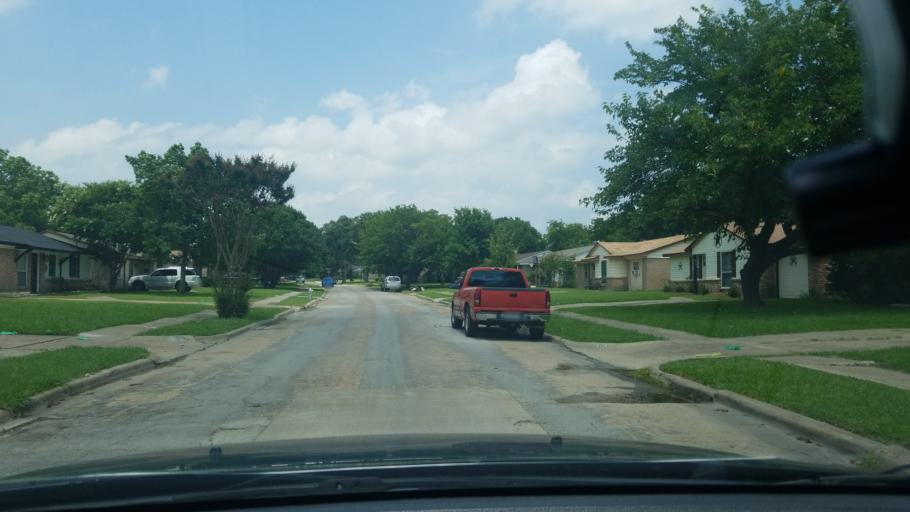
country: US
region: Texas
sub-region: Dallas County
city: Mesquite
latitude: 32.7977
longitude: -96.6418
